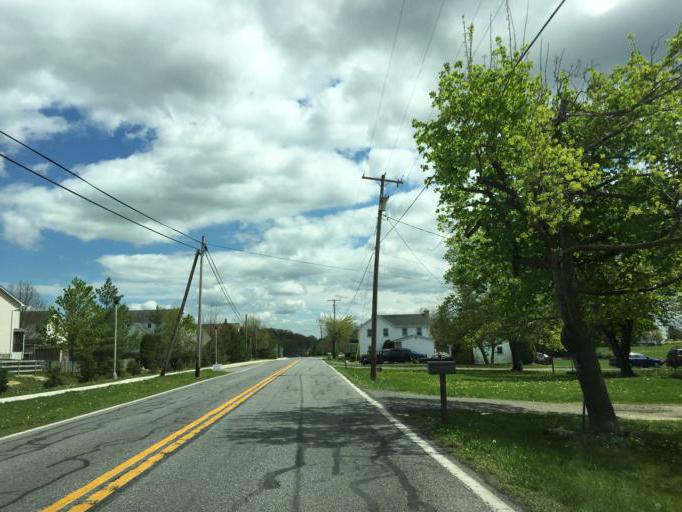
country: US
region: Maryland
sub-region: Frederick County
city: Thurmont
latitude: 39.6140
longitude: -77.3956
